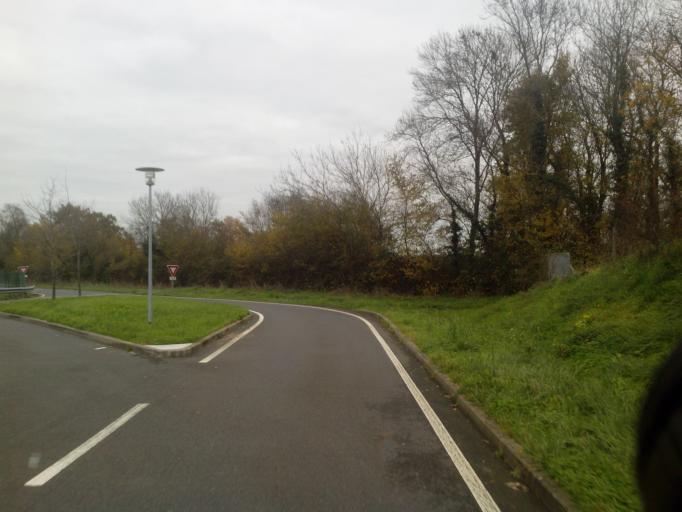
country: FR
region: Pays de la Loire
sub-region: Departement de la Loire-Atlantique
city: Le Pallet
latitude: 47.1555
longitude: -1.3118
